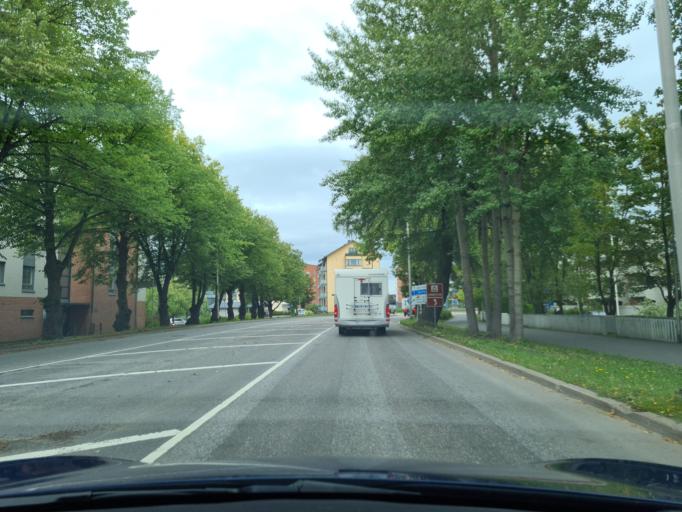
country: FI
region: South Karelia
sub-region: Lappeenranta
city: Lappeenranta
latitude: 61.0536
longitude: 28.1849
